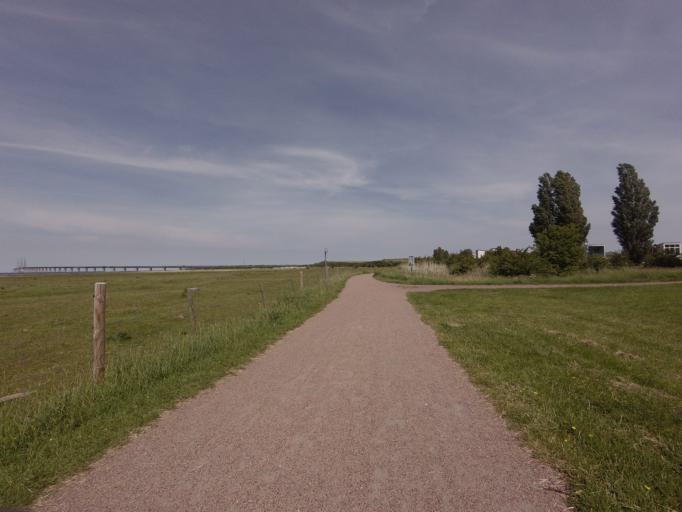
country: SE
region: Skane
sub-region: Malmo
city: Bunkeflostrand
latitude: 55.5532
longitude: 12.9085
